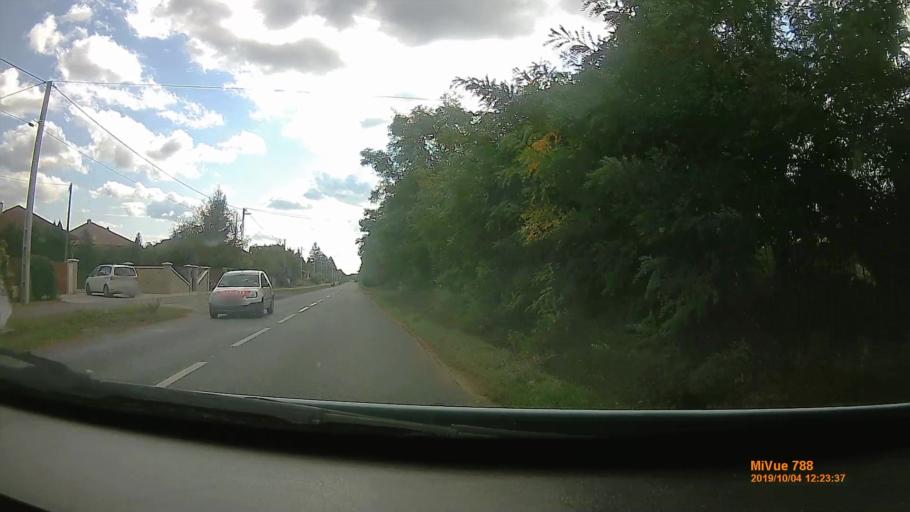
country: HU
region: Szabolcs-Szatmar-Bereg
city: Kotaj
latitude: 48.0040
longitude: 21.6985
